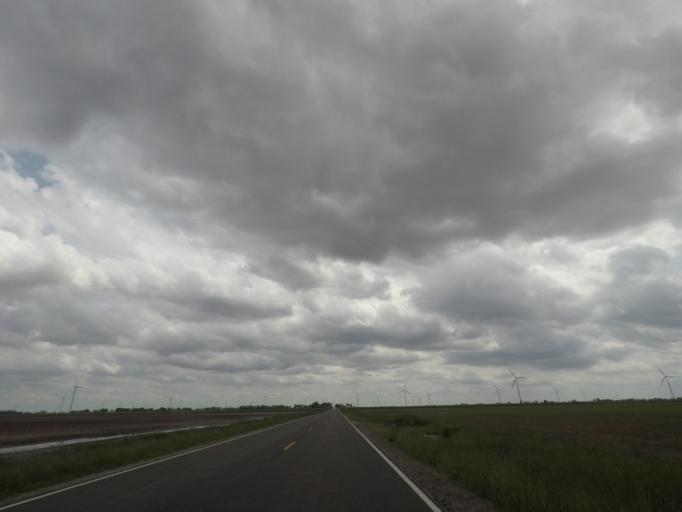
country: US
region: Illinois
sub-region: Macon County
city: Warrensburg
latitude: 40.0382
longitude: -89.0855
